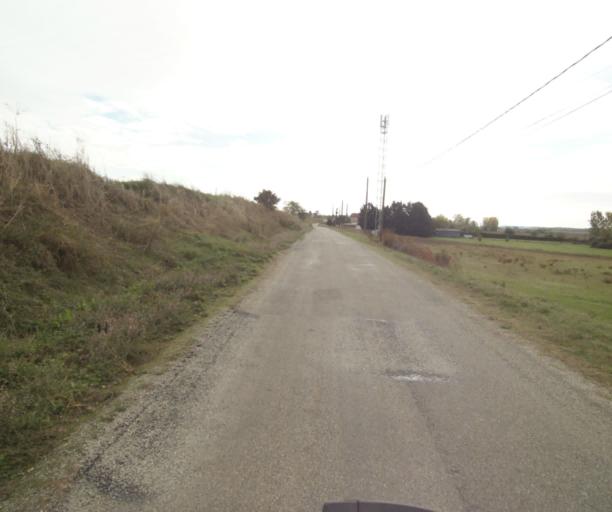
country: FR
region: Midi-Pyrenees
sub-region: Departement du Tarn-et-Garonne
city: Finhan
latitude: 43.8998
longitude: 1.2279
